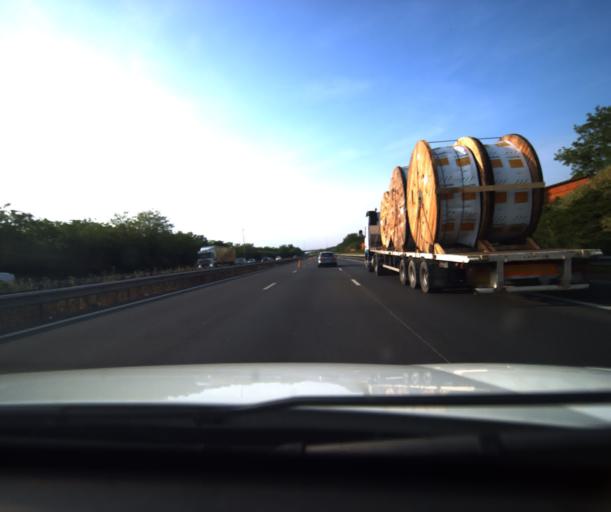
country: FR
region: Midi-Pyrenees
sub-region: Departement de la Haute-Garonne
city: Saint-Alban
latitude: 43.6843
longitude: 1.4131
